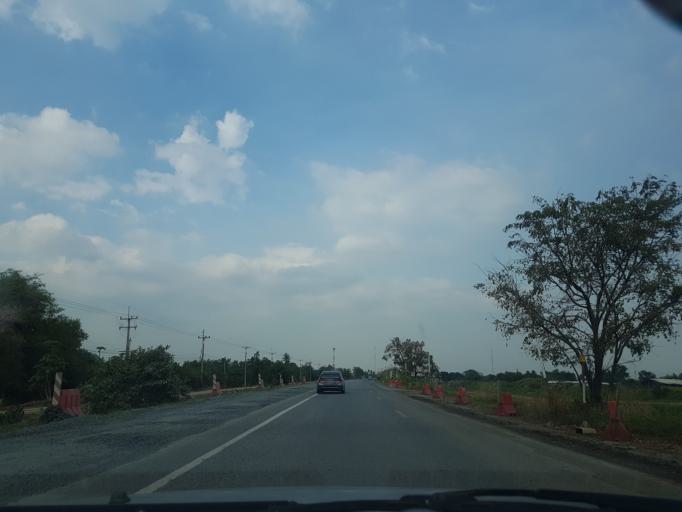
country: TH
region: Sara Buri
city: Nong Saeng
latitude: 14.4991
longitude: 100.7350
